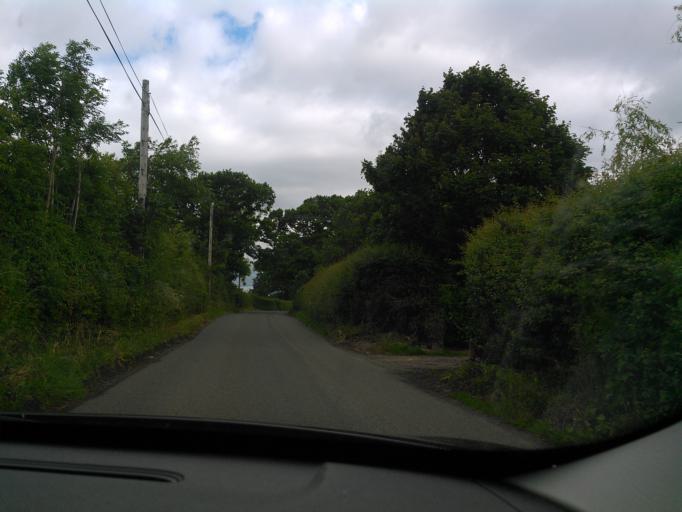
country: GB
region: England
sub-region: Shropshire
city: Wem
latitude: 52.8716
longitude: -2.7450
